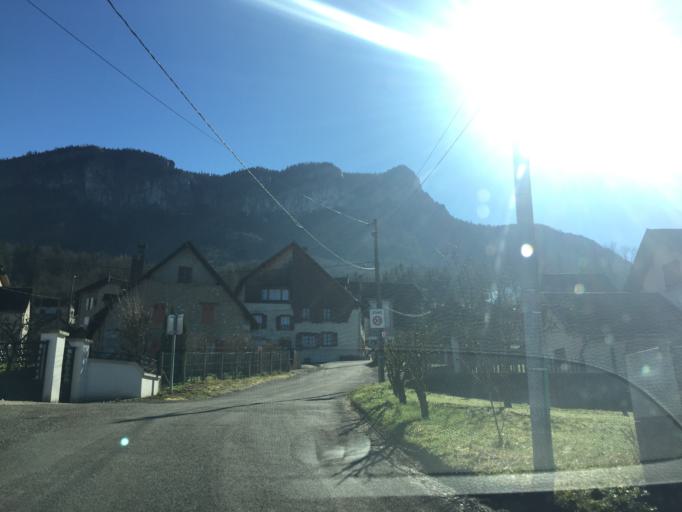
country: FR
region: Rhone-Alpes
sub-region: Departement de l'Isere
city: Saint-Laurent-du-Pont
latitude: 45.3926
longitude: 5.7441
